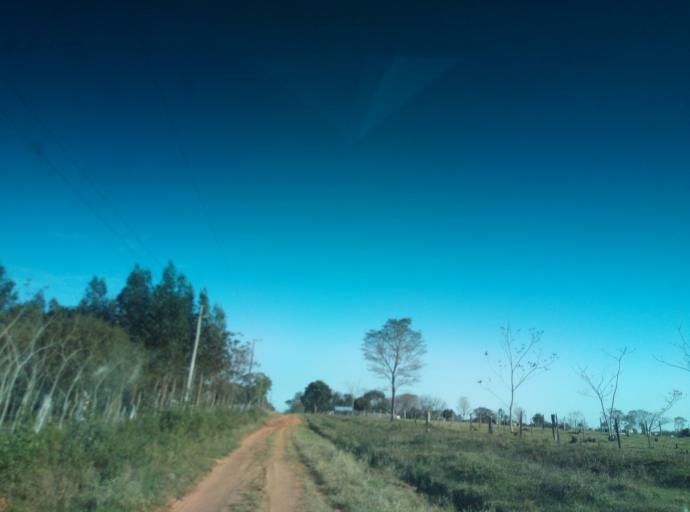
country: PY
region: Caaguazu
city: Doctor Cecilio Baez
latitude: -25.1684
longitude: -56.2320
